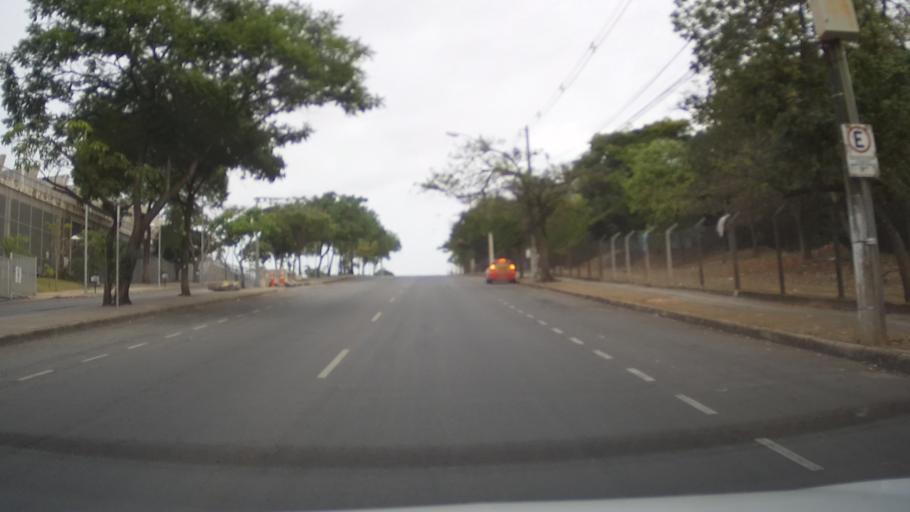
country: BR
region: Minas Gerais
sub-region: Belo Horizonte
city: Belo Horizonte
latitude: -19.8670
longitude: -43.9689
